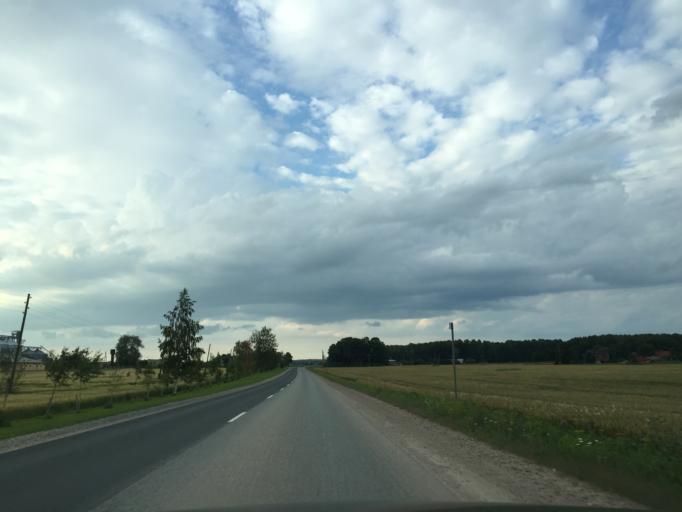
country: LV
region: Dobeles Rajons
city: Dobele
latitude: 56.7210
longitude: 23.3856
